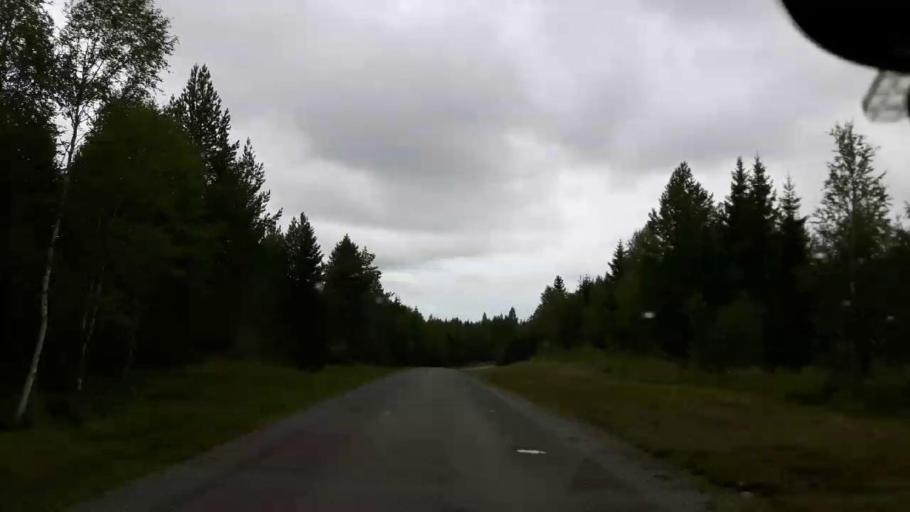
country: SE
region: Jaemtland
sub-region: OEstersunds Kommun
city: Ostersund
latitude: 63.0638
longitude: 14.5524
